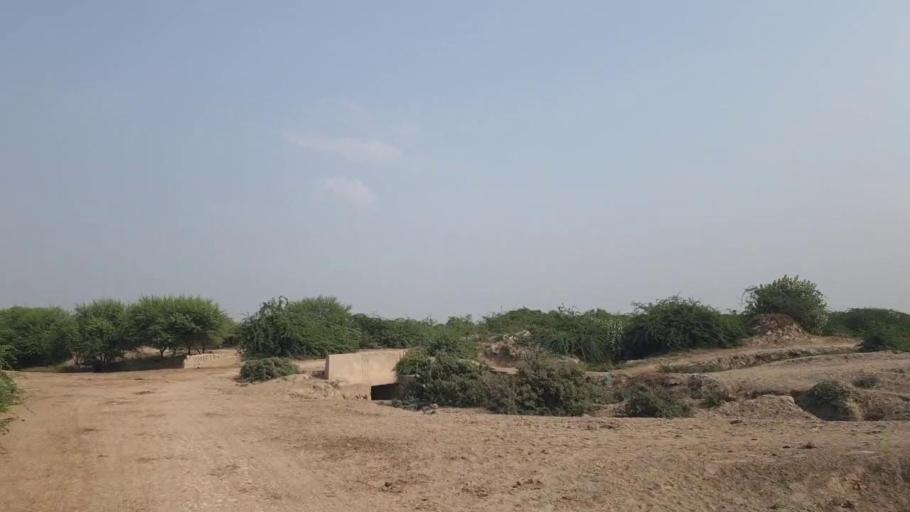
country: PK
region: Sindh
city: Badin
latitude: 24.5475
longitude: 68.7031
